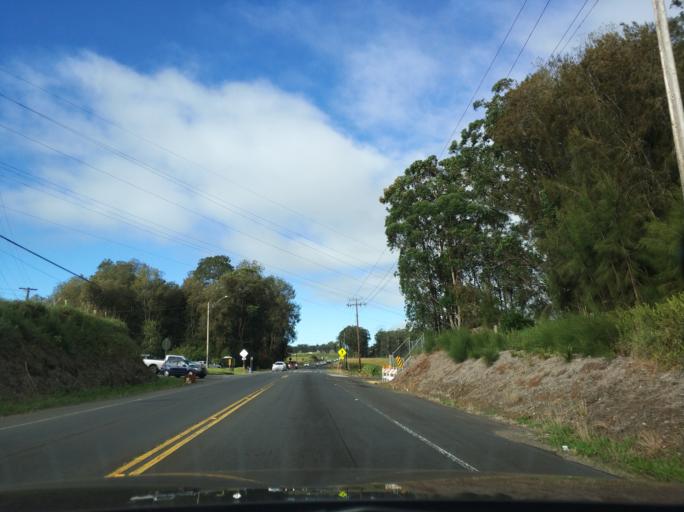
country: US
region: Hawaii
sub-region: Hawaii County
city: Waimea
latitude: 20.0428
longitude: -155.5967
